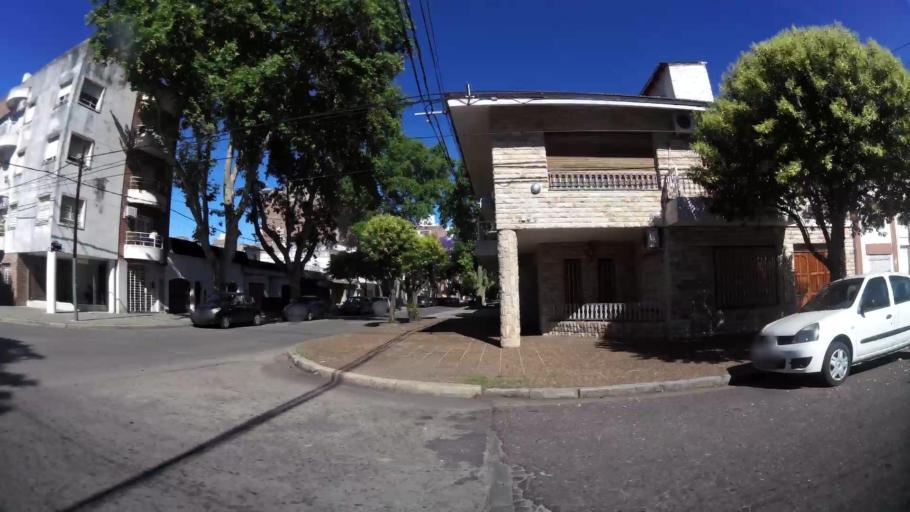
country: AR
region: Santa Fe
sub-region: Departamento de Rosario
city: Rosario
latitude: -32.9497
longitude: -60.6761
